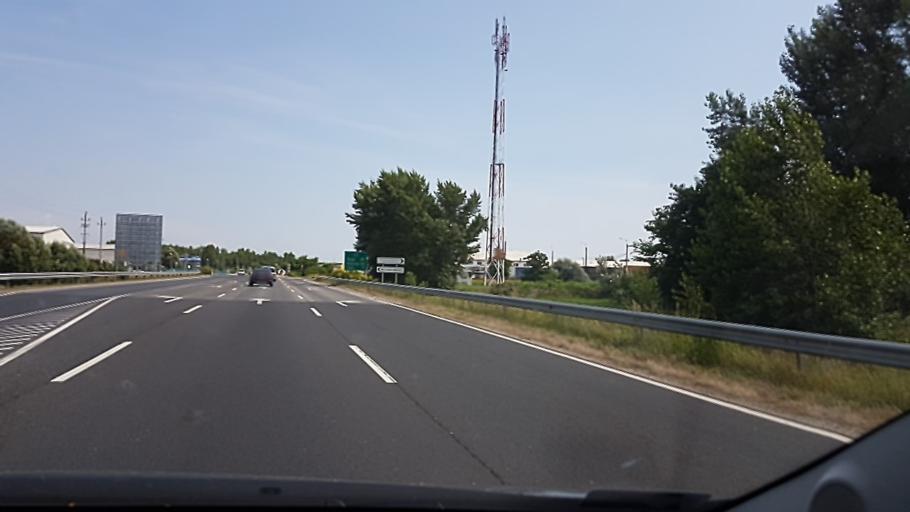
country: HU
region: Pest
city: Dunaharaszti
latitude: 47.3643
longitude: 19.1175
